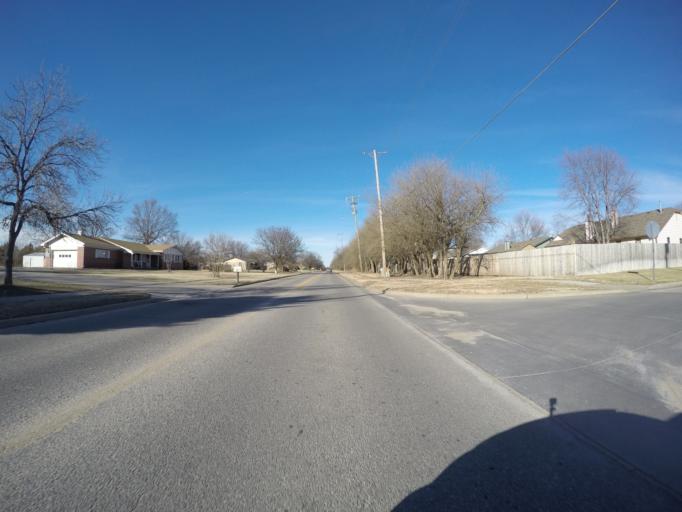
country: US
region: Kansas
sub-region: Sedgwick County
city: Maize
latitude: 37.6949
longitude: -97.4807
